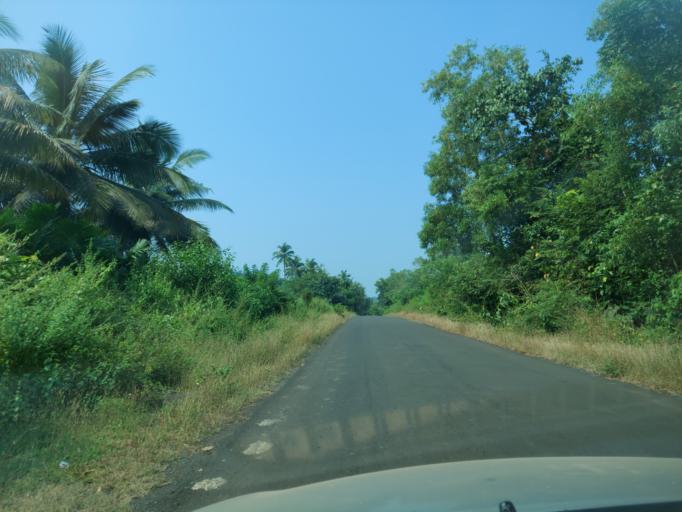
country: IN
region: Maharashtra
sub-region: Sindhudurg
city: Kudal
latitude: 15.9755
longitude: 73.6219
